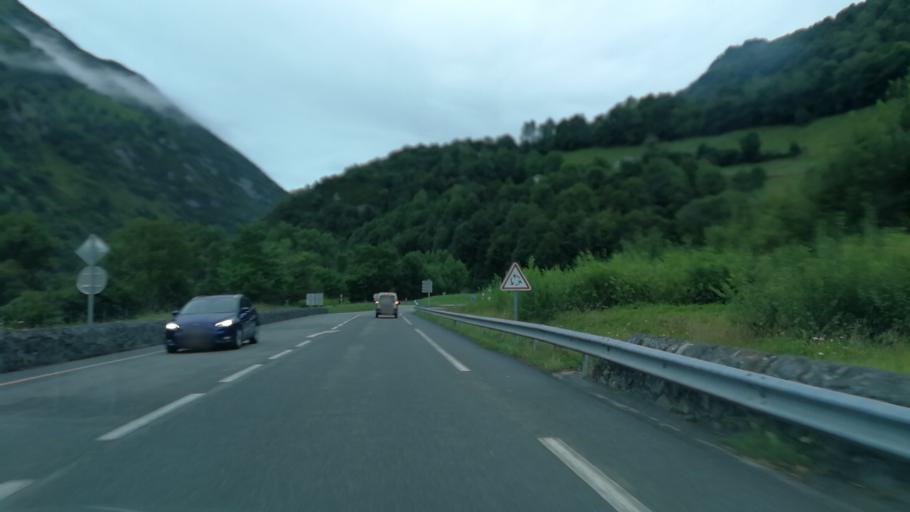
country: FR
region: Aquitaine
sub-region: Departement des Pyrenees-Atlantiques
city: Arette
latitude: 43.0093
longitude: -0.6032
